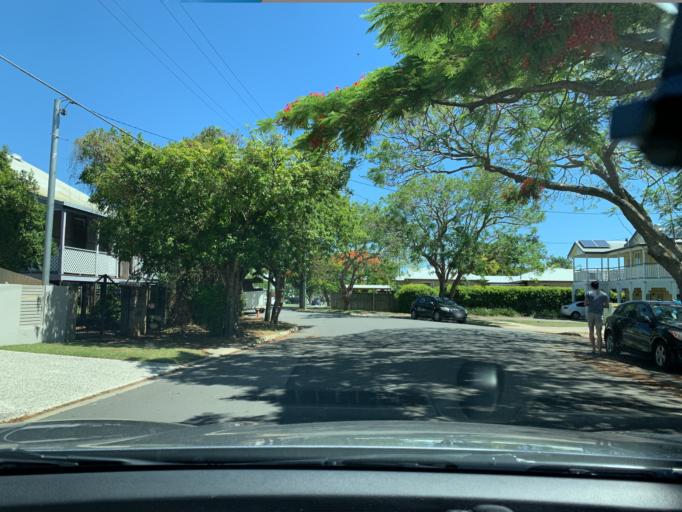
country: AU
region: Queensland
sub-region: Brisbane
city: Ascot
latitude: -27.4214
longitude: 153.0719
